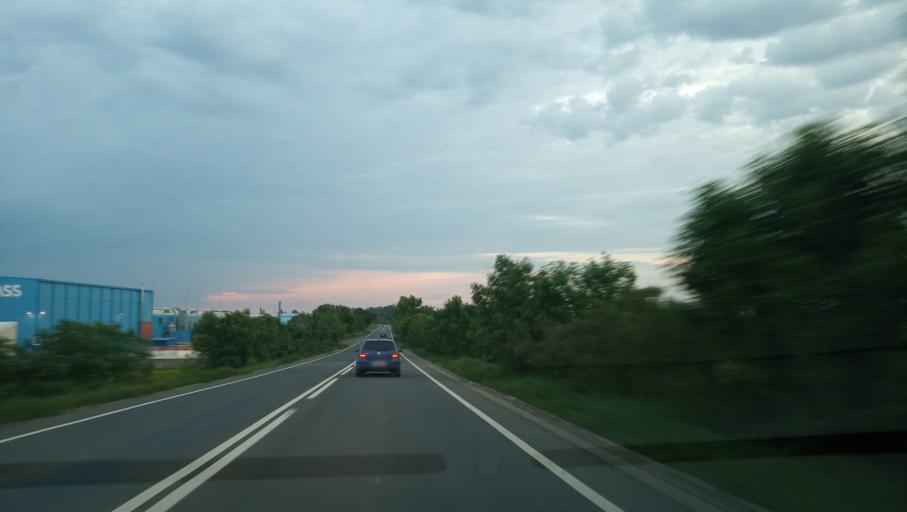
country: RO
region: Timis
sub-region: Comuna Sag
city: Sag
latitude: 45.6285
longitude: 21.1897
